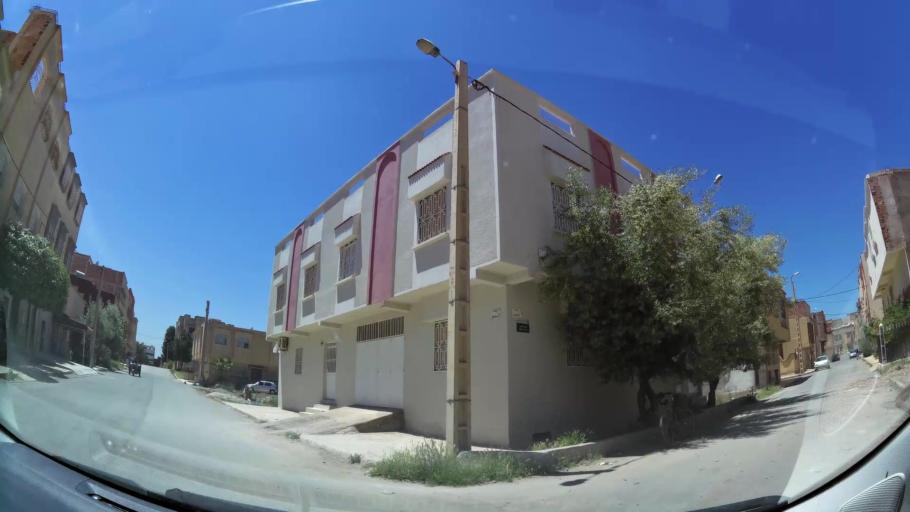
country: MA
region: Oriental
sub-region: Oujda-Angad
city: Oujda
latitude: 34.6808
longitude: -1.8715
